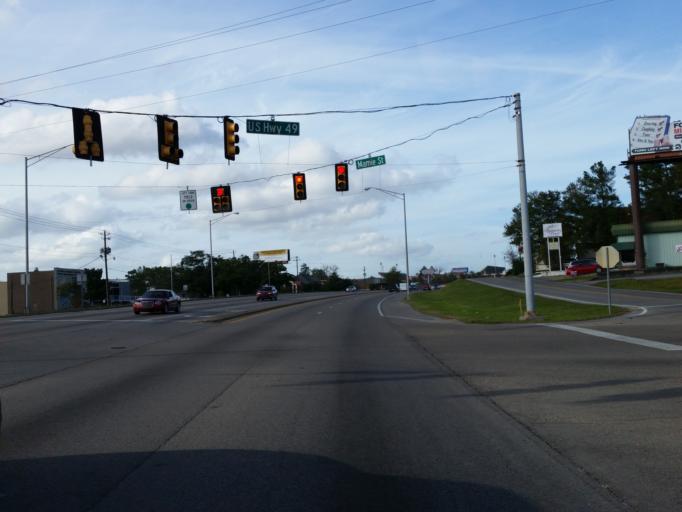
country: US
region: Mississippi
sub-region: Forrest County
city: Hattiesburg
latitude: 31.3192
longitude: -89.3282
